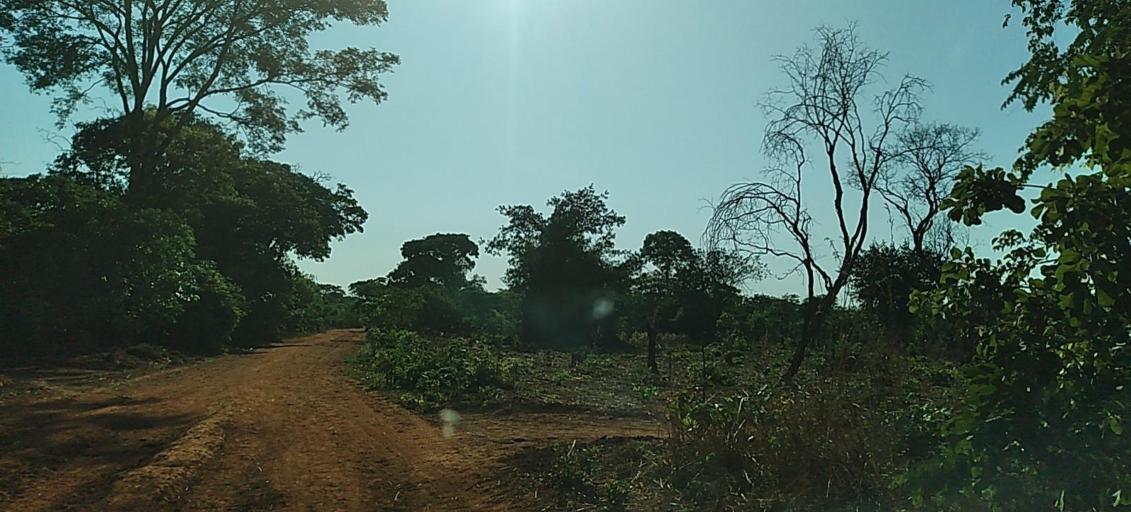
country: ZM
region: Copperbelt
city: Luanshya
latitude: -13.4591
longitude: 28.8173
